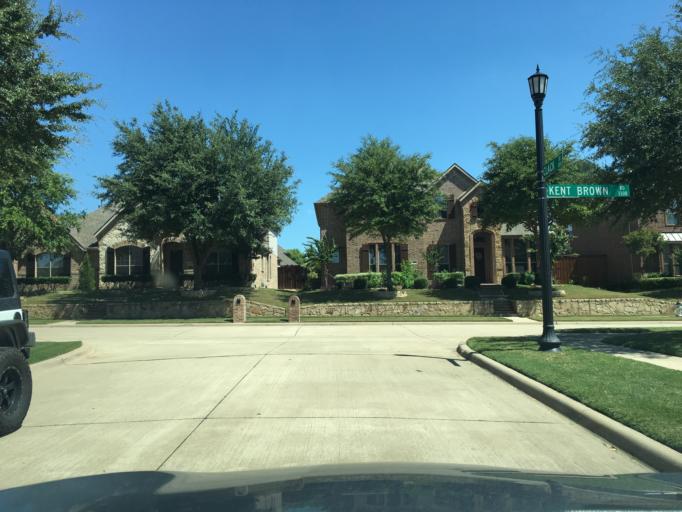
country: US
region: Texas
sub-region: Dallas County
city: Sachse
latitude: 32.9666
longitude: -96.6165
